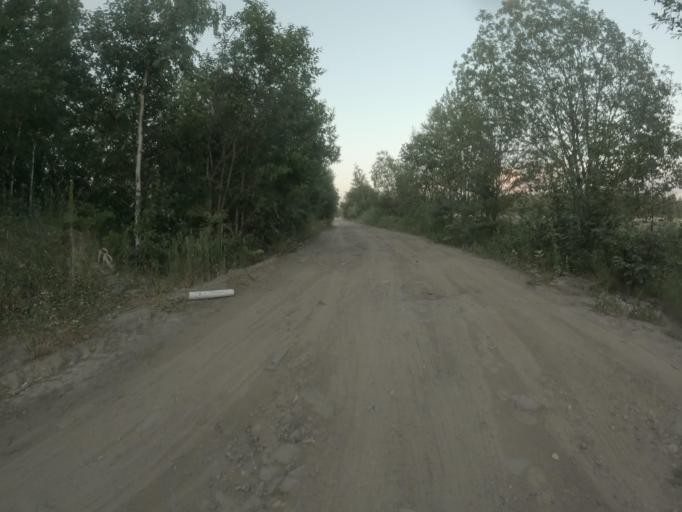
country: RU
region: Leningrad
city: Yanino Vtoroye
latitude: 59.9580
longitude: 30.5612
